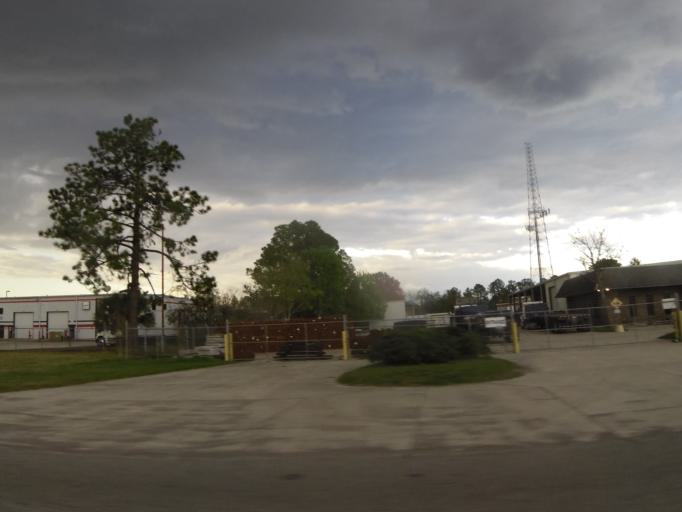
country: US
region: Florida
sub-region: Saint Johns County
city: Fruit Cove
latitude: 30.1894
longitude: -81.5686
